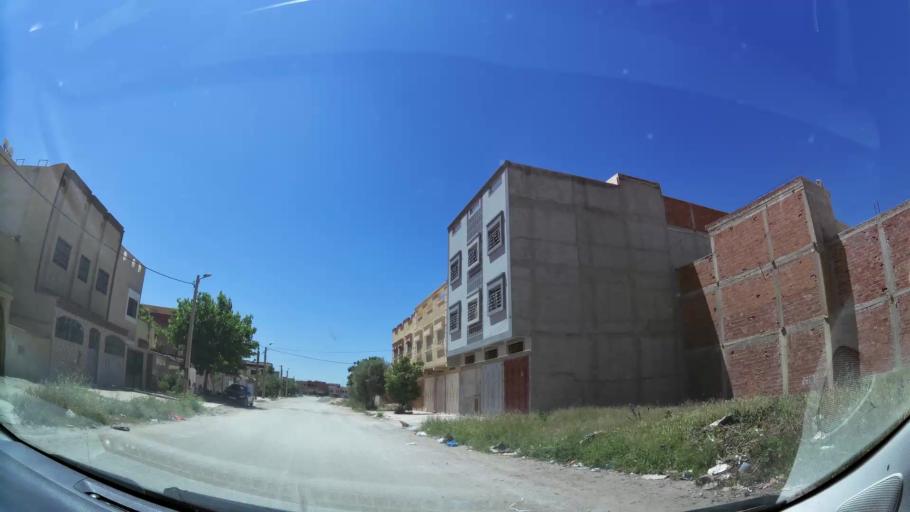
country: MA
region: Oriental
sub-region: Oujda-Angad
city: Oujda
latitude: 34.6780
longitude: -1.8569
